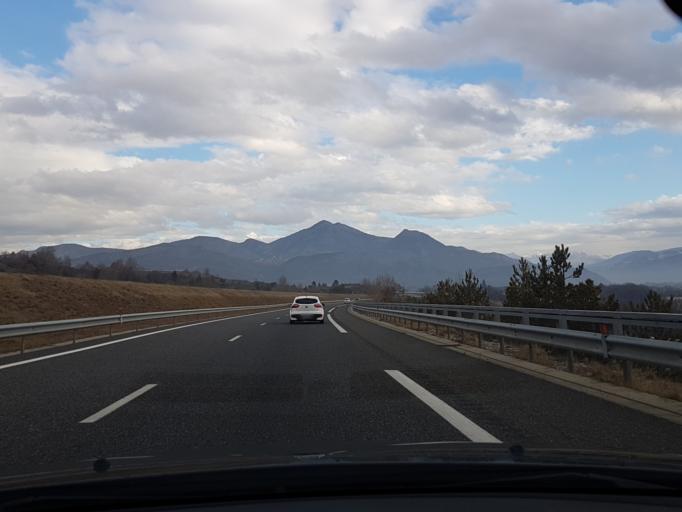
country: FR
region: Provence-Alpes-Cote d'Azur
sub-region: Departement des Hautes-Alpes
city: Tallard
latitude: 44.3999
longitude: 5.9486
